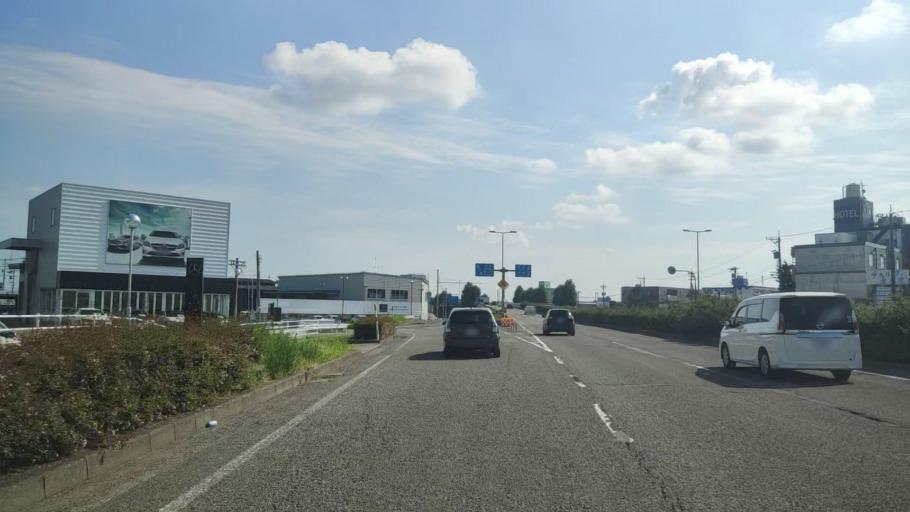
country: JP
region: Ishikawa
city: Nonoichi
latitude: 36.5303
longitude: 136.5931
